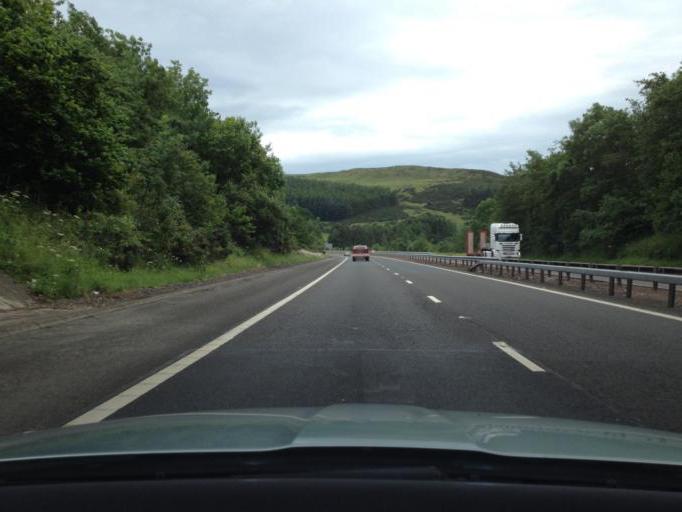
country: GB
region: Scotland
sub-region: Perth and Kinross
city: Bridge of Earn
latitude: 56.3268
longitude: -3.3982
